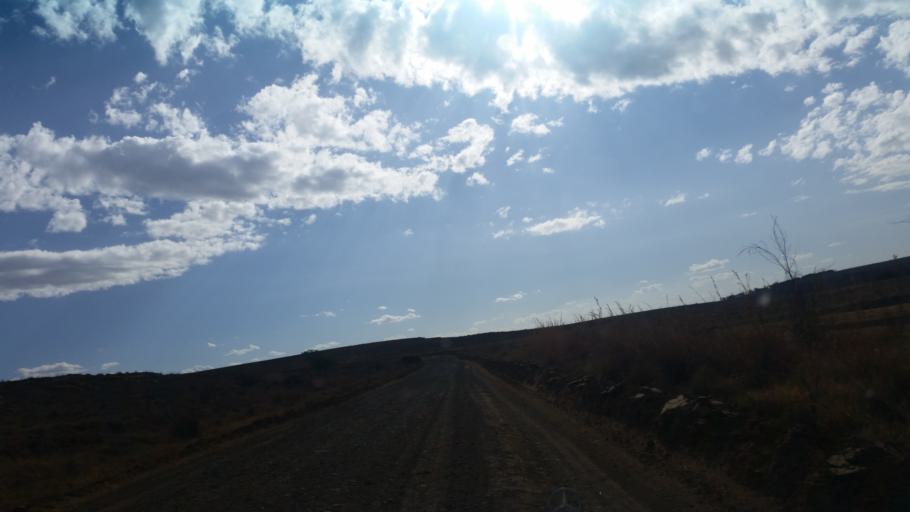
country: ZA
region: Orange Free State
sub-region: Thabo Mofutsanyana District Municipality
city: Phuthaditjhaba
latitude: -28.3506
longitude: 28.6083
